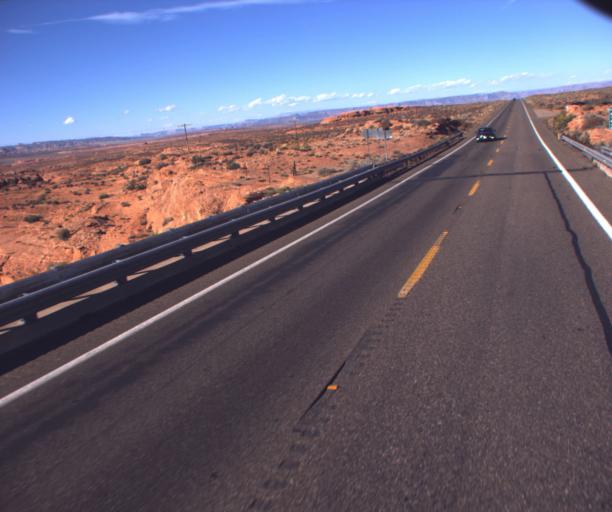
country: US
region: Arizona
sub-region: Coconino County
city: LeChee
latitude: 36.8368
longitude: -111.5084
